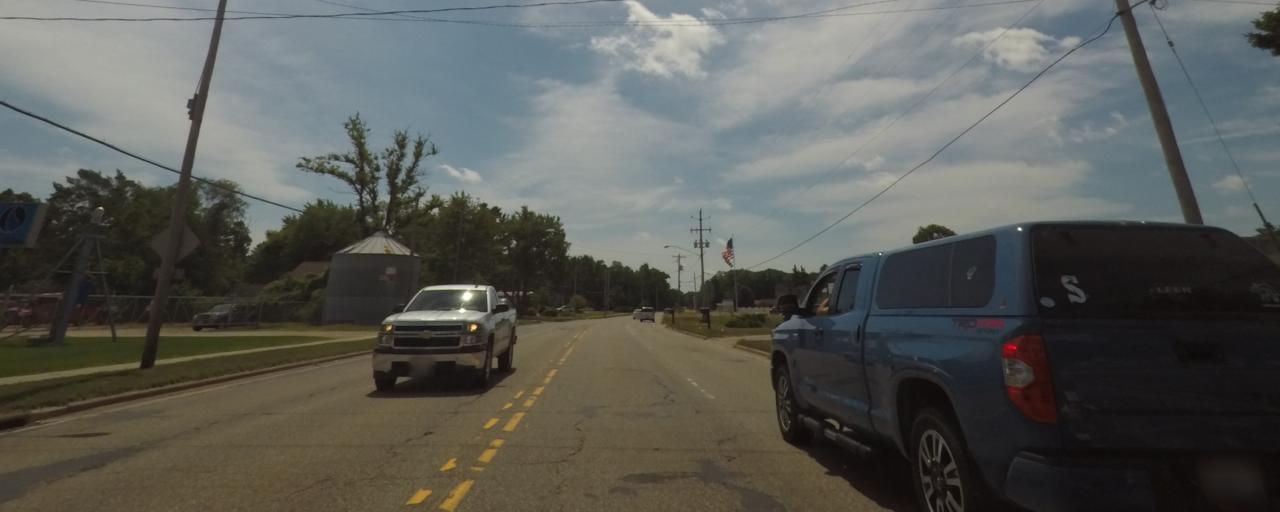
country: US
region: Wisconsin
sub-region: Portage County
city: Plover
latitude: 44.4760
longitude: -89.5479
